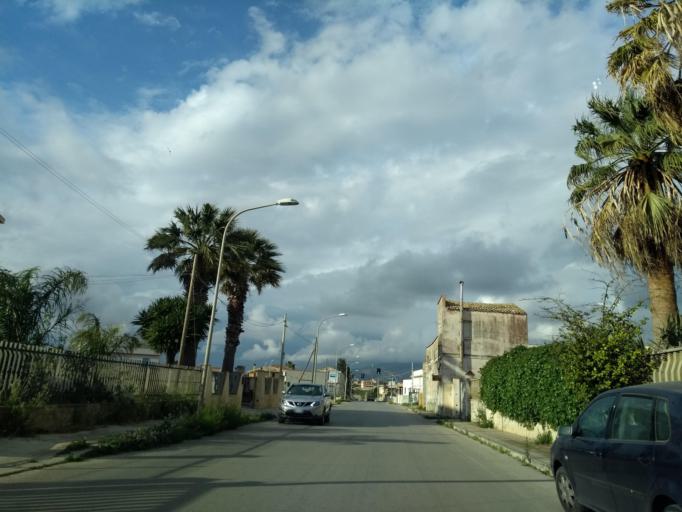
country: IT
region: Sicily
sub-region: Trapani
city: Marausa
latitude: 37.9440
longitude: 12.5116
